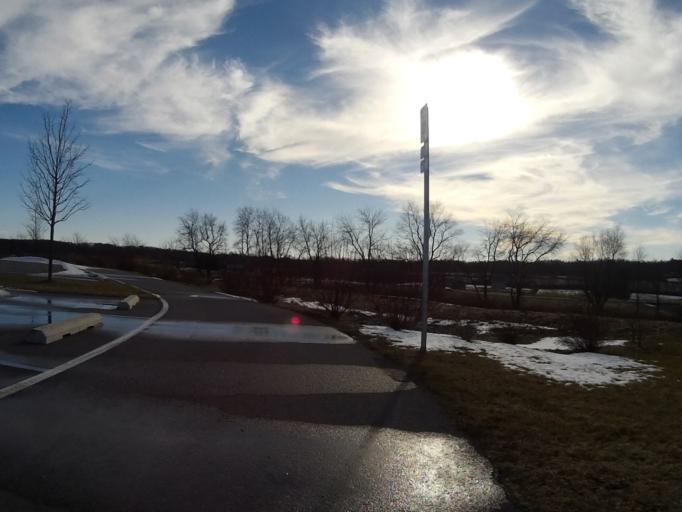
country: US
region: Pennsylvania
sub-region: Centre County
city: Houserville
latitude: 40.8486
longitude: -77.8768
